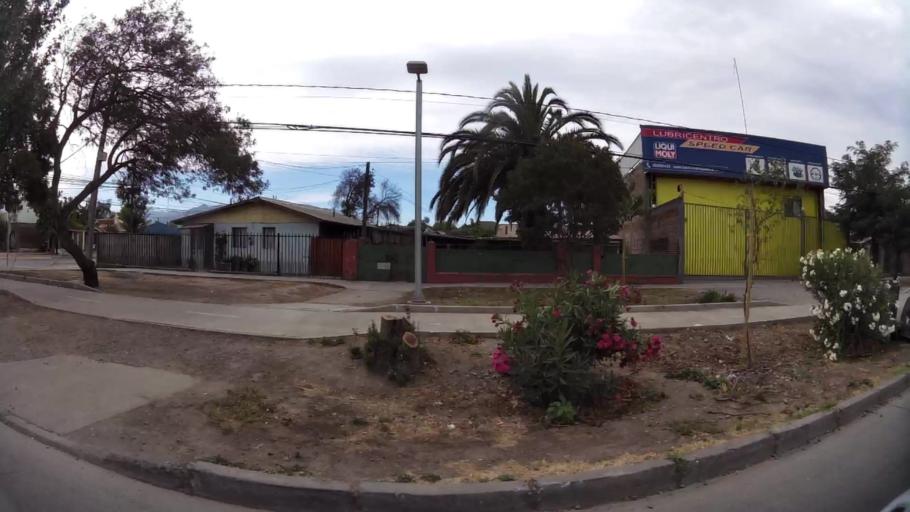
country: CL
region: O'Higgins
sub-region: Provincia de Cachapoal
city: Rancagua
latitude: -34.1462
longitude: -70.7355
